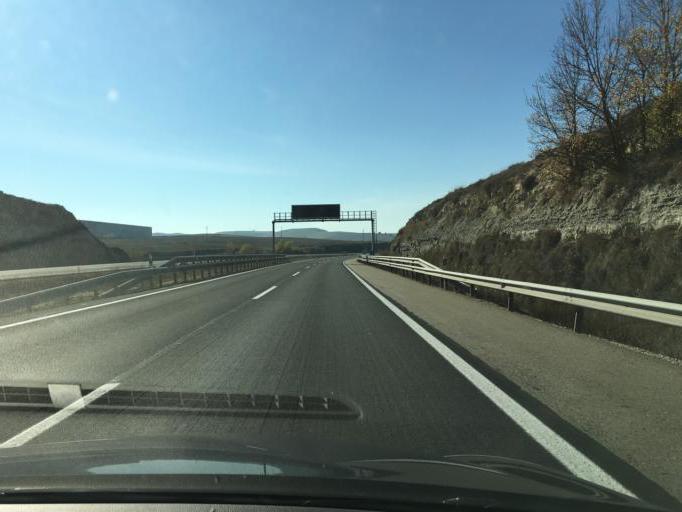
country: ES
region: Castille and Leon
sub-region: Provincia de Burgos
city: Briviesca
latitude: 42.5353
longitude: -3.3105
